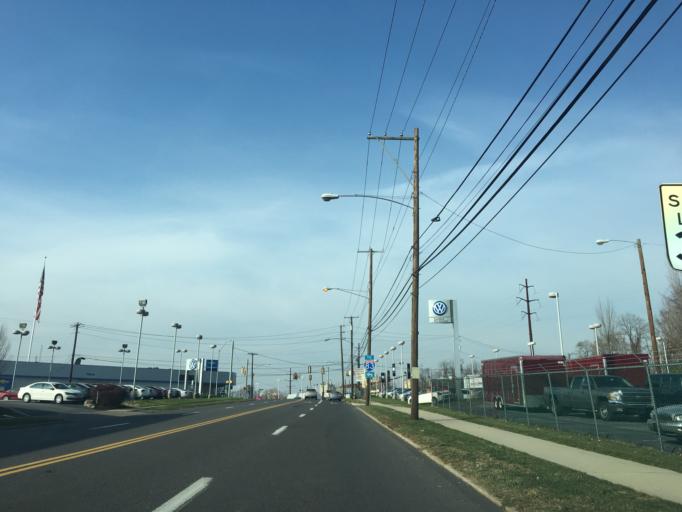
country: US
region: Pennsylvania
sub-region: Dauphin County
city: Penbrook
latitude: 40.2557
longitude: -76.8639
